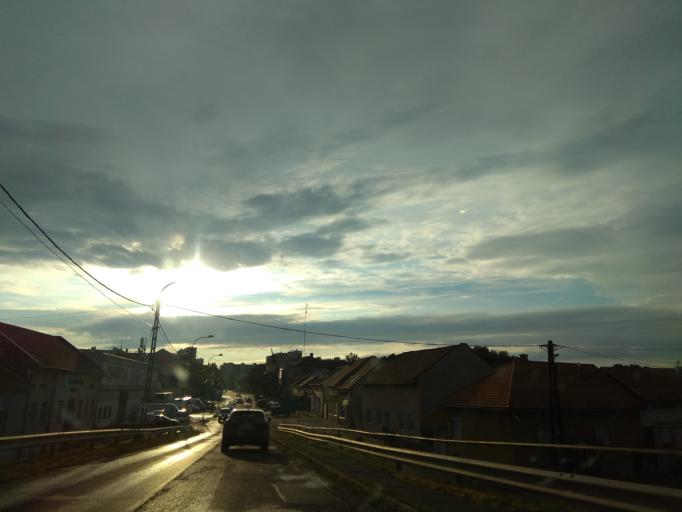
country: HU
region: Borsod-Abauj-Zemplen
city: Miskolc
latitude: 48.0987
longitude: 20.8008
